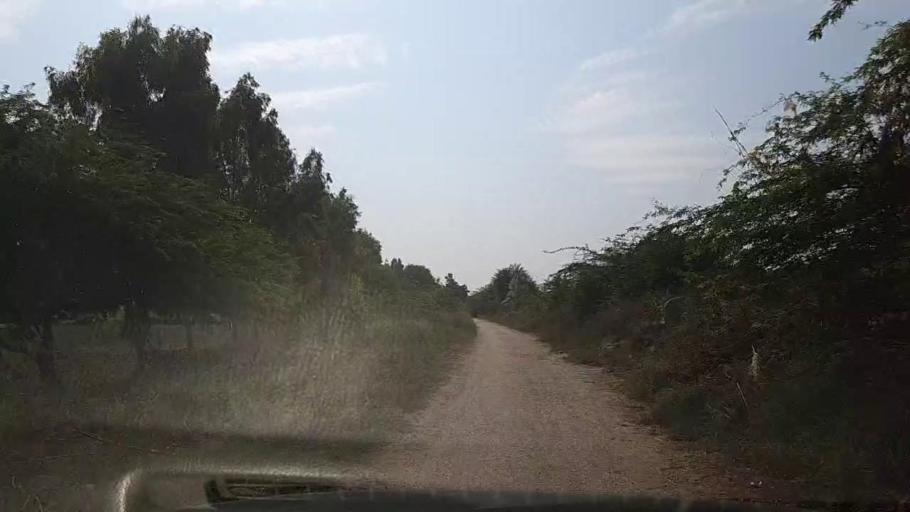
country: PK
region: Sindh
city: Thatta
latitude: 24.7610
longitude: 67.7797
